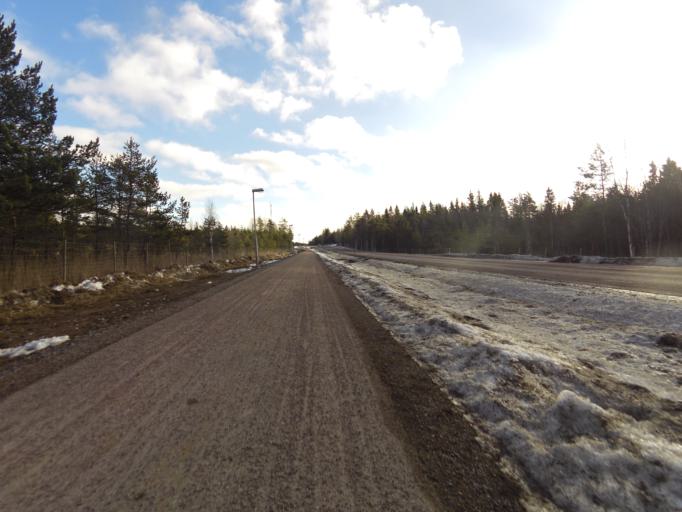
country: SE
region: Gaevleborg
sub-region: Gavle Kommun
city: Gavle
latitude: 60.6499
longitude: 17.2331
